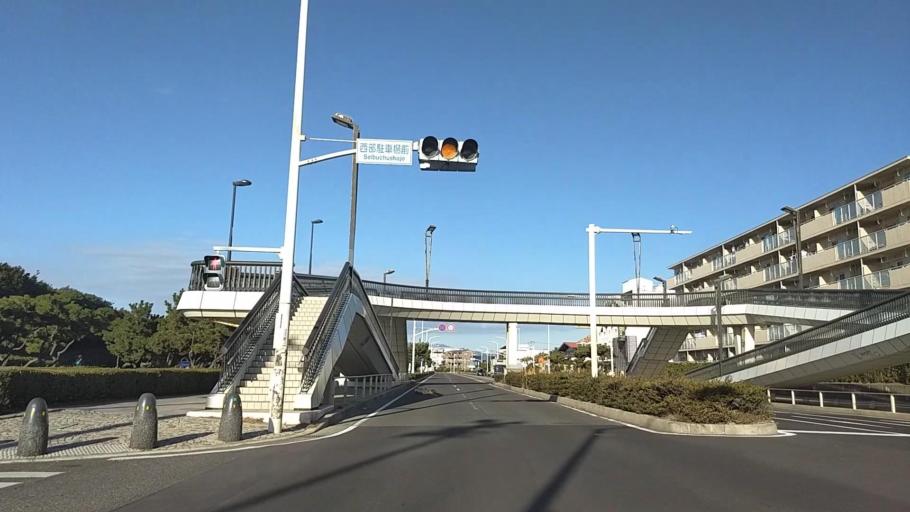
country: JP
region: Kanagawa
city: Fujisawa
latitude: 35.3151
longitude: 139.4738
